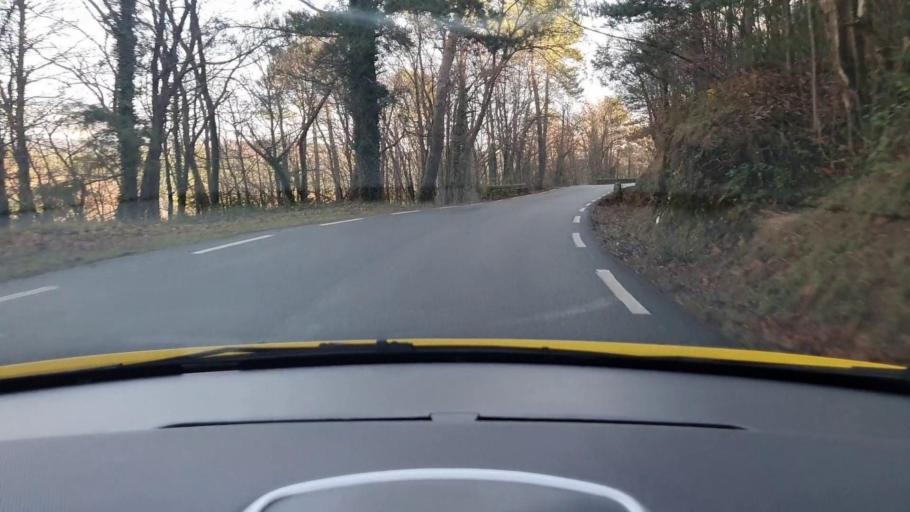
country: FR
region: Languedoc-Roussillon
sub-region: Departement du Gard
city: Branoux-les-Taillades
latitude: 44.3341
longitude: 3.9589
